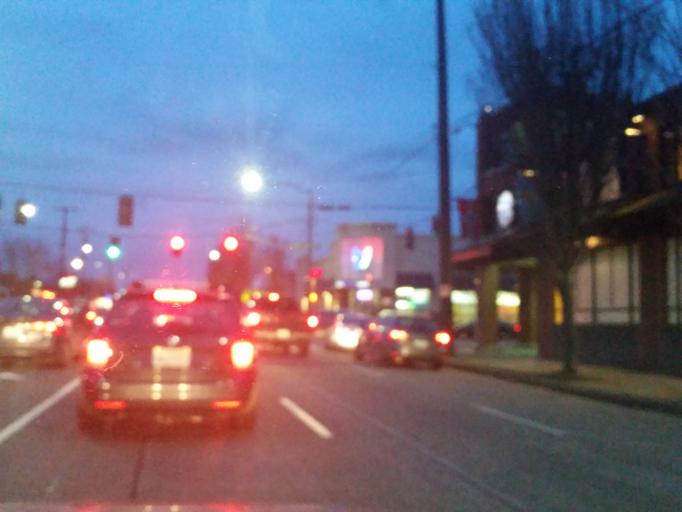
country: US
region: Washington
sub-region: King County
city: Shoreline
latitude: 47.6903
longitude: -122.3767
